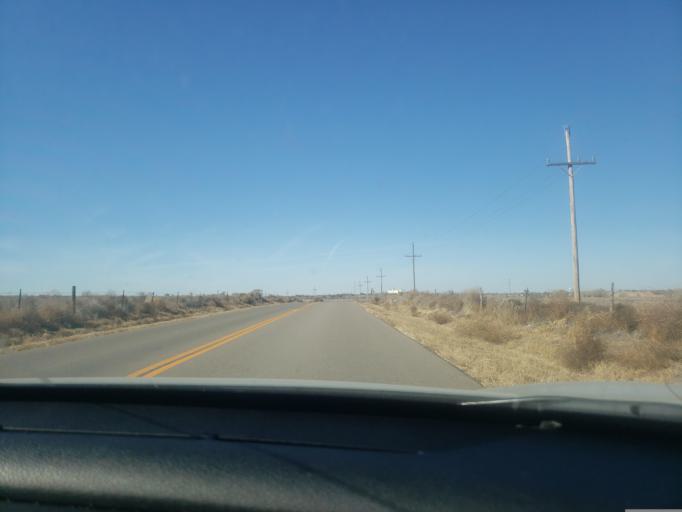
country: US
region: Kansas
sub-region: Finney County
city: Garden City
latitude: 37.9489
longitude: -100.8512
